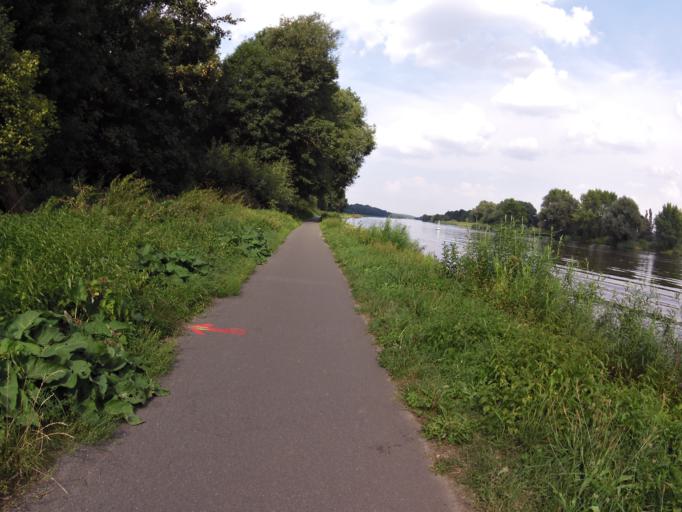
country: DE
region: North Rhine-Westphalia
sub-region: Regierungsbezirk Detmold
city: Minden
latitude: 52.3219
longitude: 8.9230
